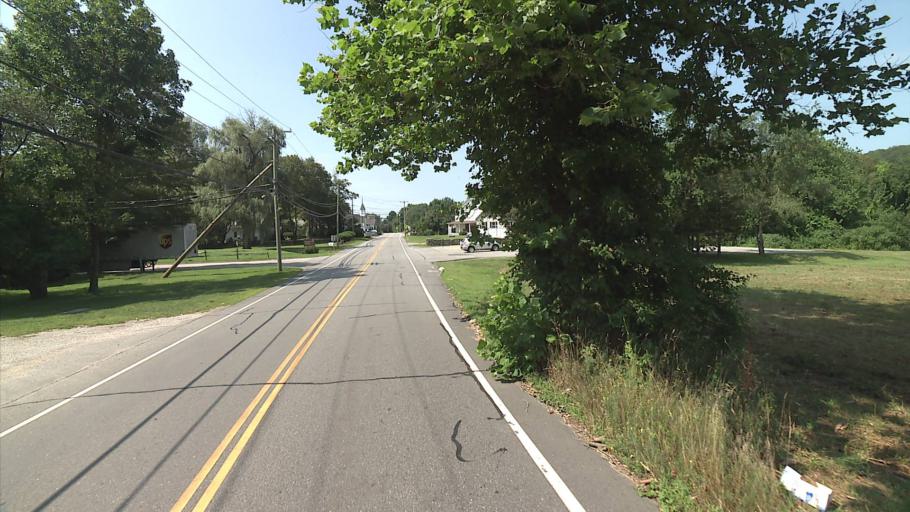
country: US
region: Connecticut
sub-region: New London County
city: Baltic
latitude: 41.5666
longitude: -72.1516
